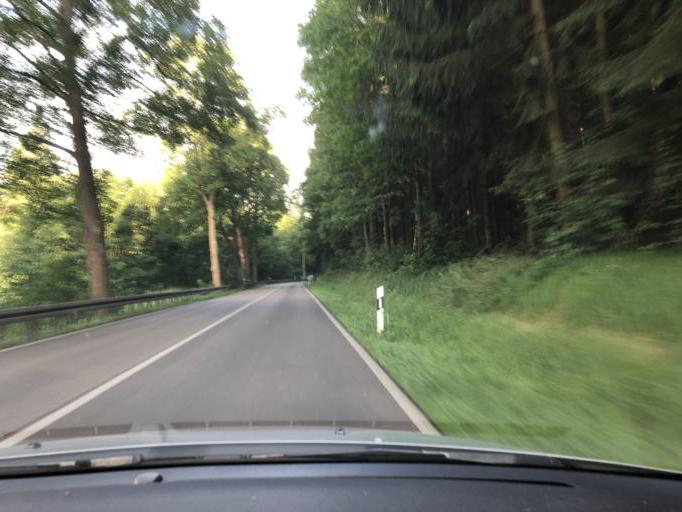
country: DE
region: Saxony
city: Bannewitz
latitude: 50.9865
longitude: 13.6938
